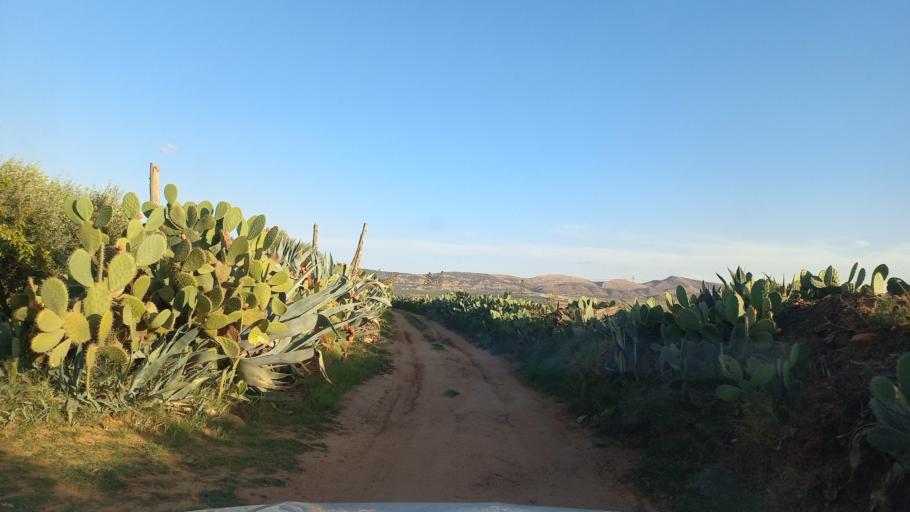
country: TN
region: Al Qasrayn
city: Sbiba
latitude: 35.4182
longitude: 9.1311
